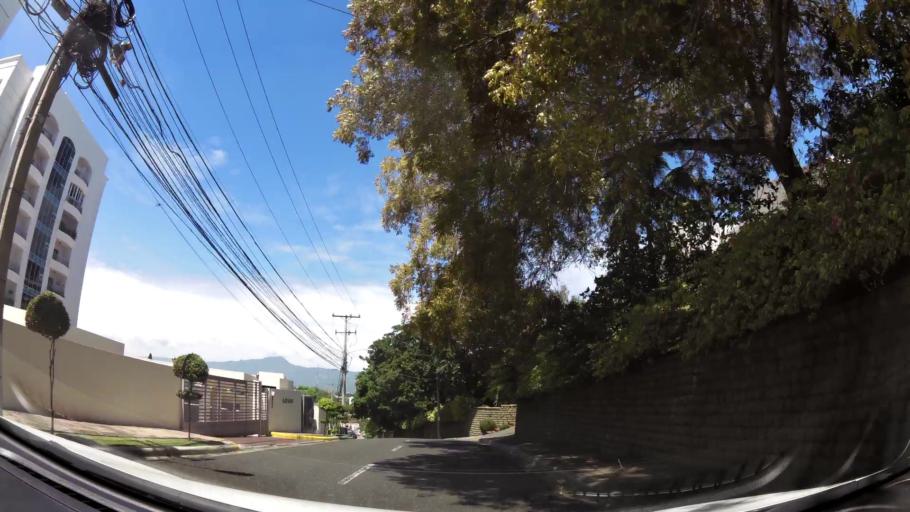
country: DO
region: Santiago
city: Santiago de los Caballeros
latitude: 19.4562
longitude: -70.6917
